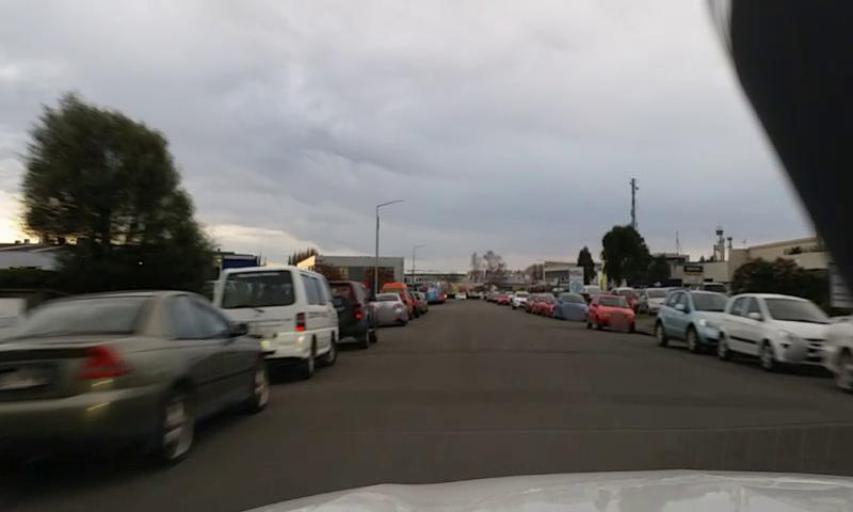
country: NZ
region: Canterbury
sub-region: Christchurch City
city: Christchurch
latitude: -43.4902
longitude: 172.5613
